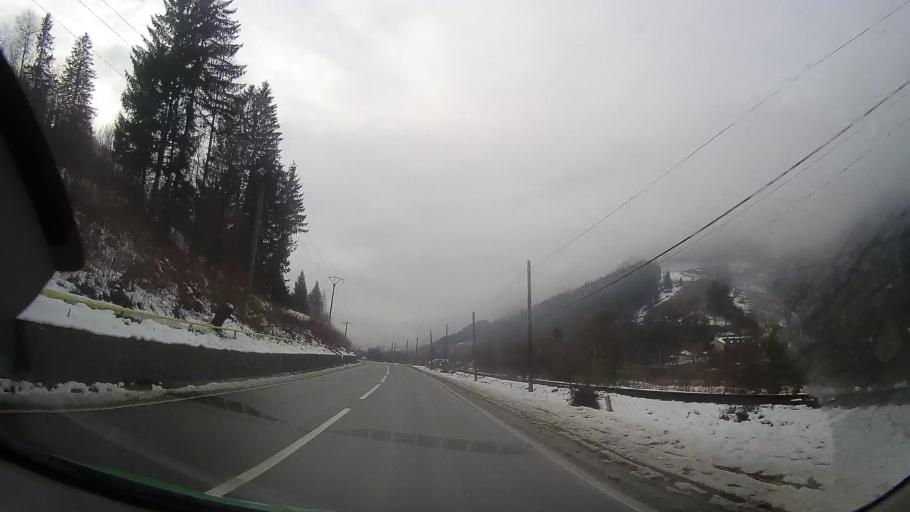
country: RO
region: Neamt
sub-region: Comuna Tasca
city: Tasca
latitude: 46.8872
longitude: 26.0072
